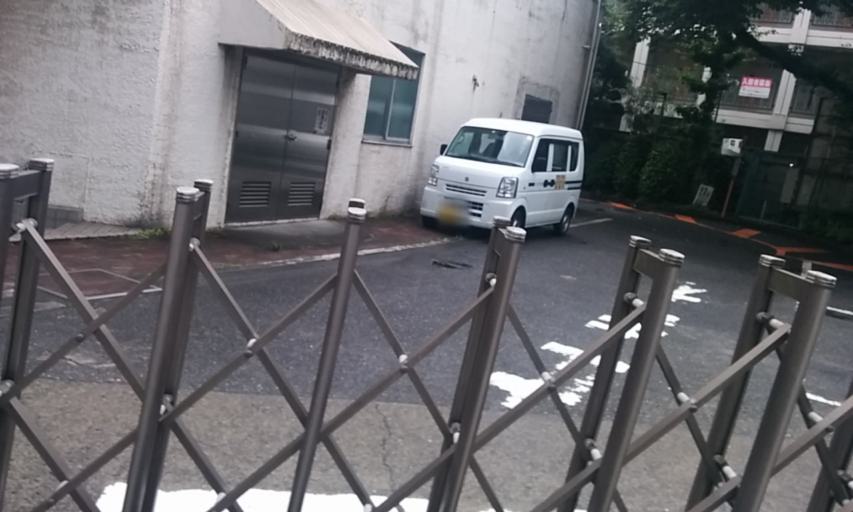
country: JP
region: Tokyo
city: Hachioji
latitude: 35.6573
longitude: 139.3417
